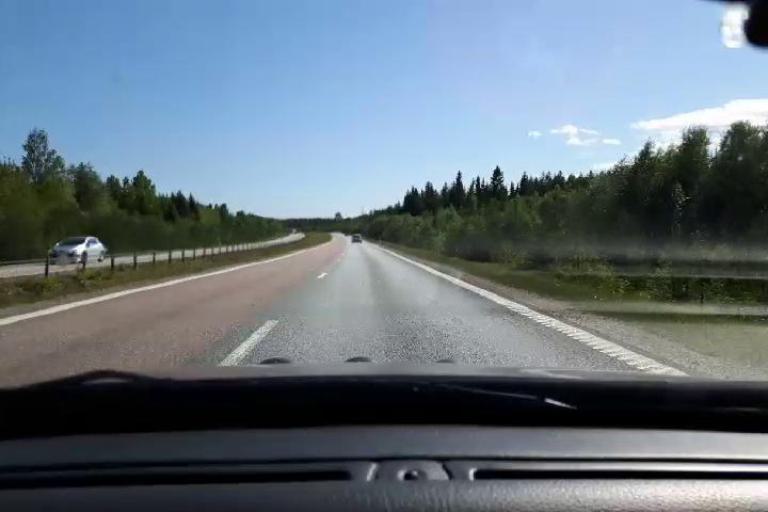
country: SE
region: Gaevleborg
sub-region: Hudiksvalls Kommun
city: Iggesund
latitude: 61.4961
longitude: 16.9845
